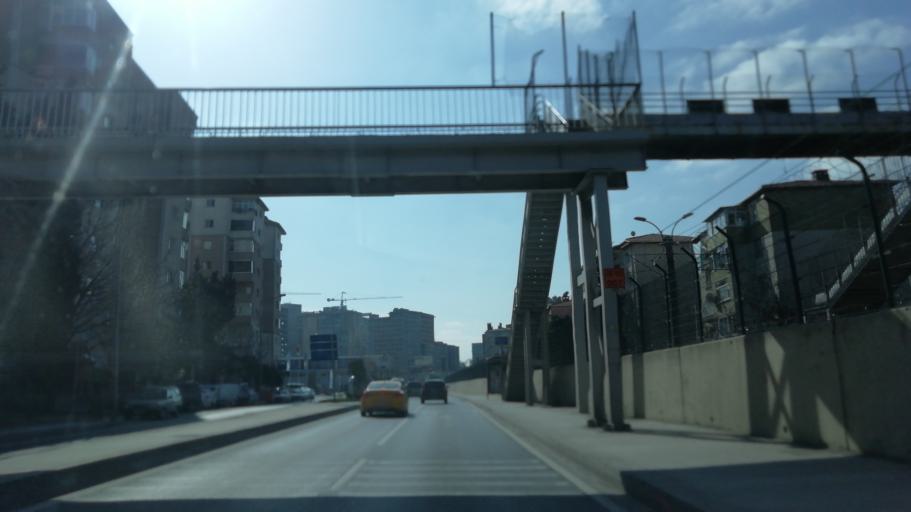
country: TR
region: Istanbul
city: merter keresteciler
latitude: 41.0157
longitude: 28.9003
